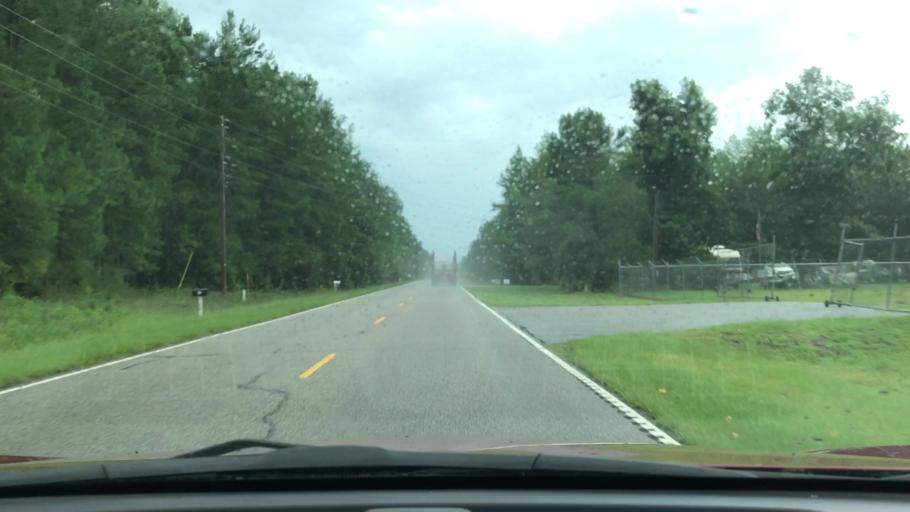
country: US
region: South Carolina
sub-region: Georgetown County
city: Georgetown
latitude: 33.4966
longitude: -79.2613
